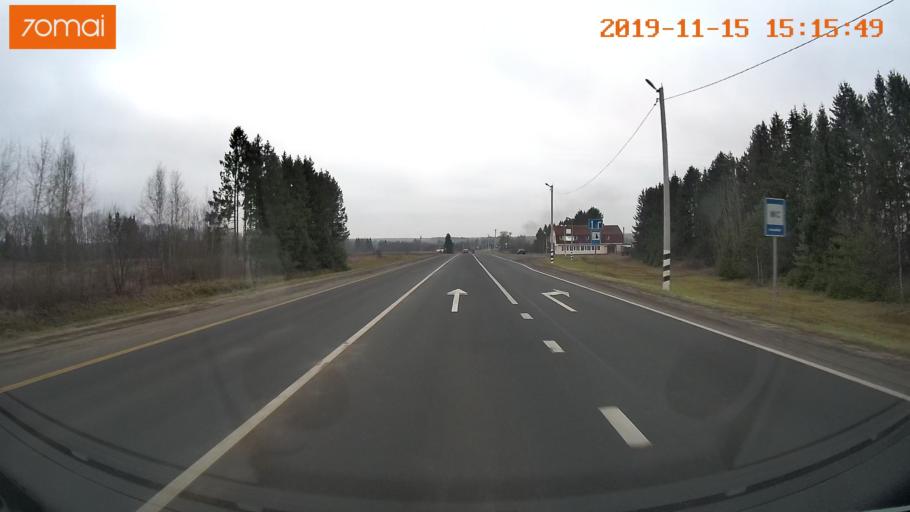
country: RU
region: Jaroslavl
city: Danilov
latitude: 58.2793
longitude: 40.1968
